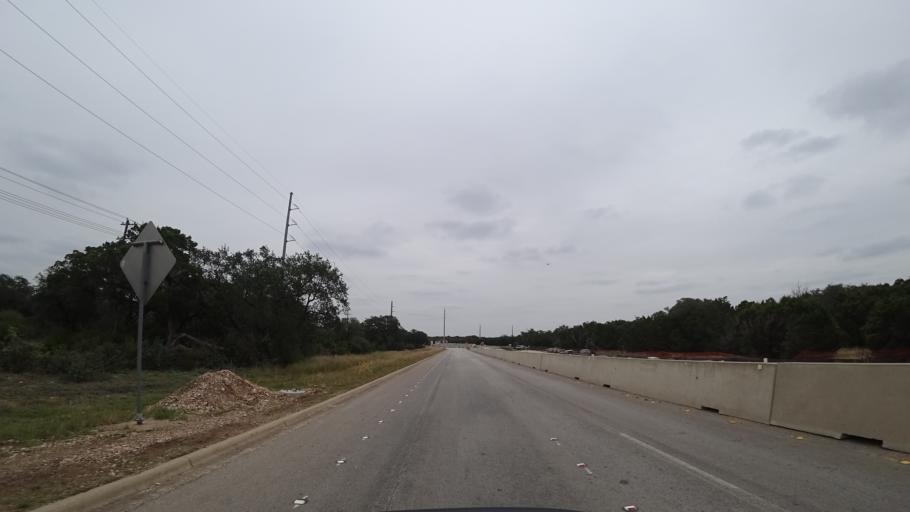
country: US
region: Texas
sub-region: Travis County
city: Shady Hollow
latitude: 30.1767
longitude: -97.8915
